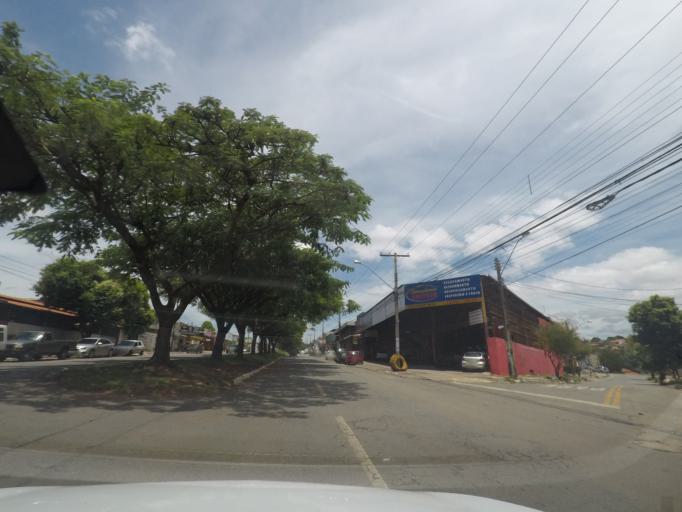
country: BR
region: Goias
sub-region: Goiania
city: Goiania
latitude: -16.6663
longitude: -49.2169
